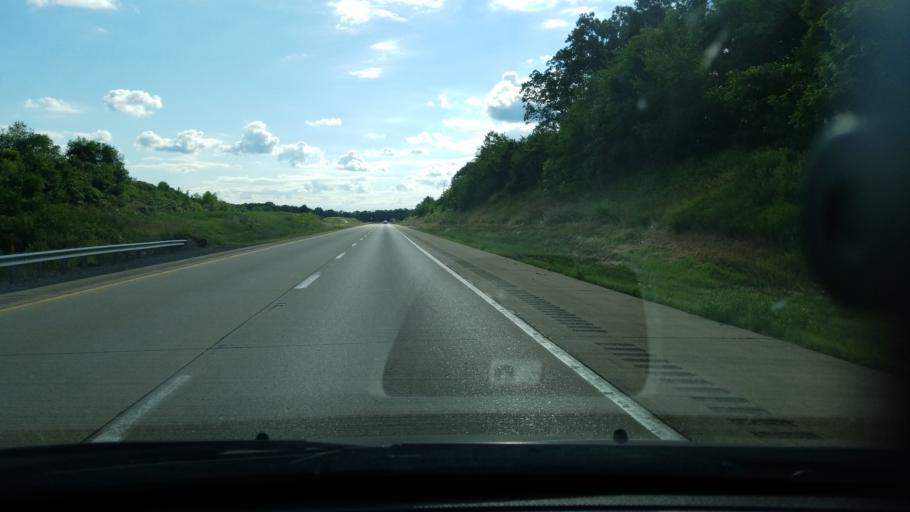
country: US
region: Pennsylvania
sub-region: Northumberland County
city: Riverside
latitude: 40.9870
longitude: -76.7078
